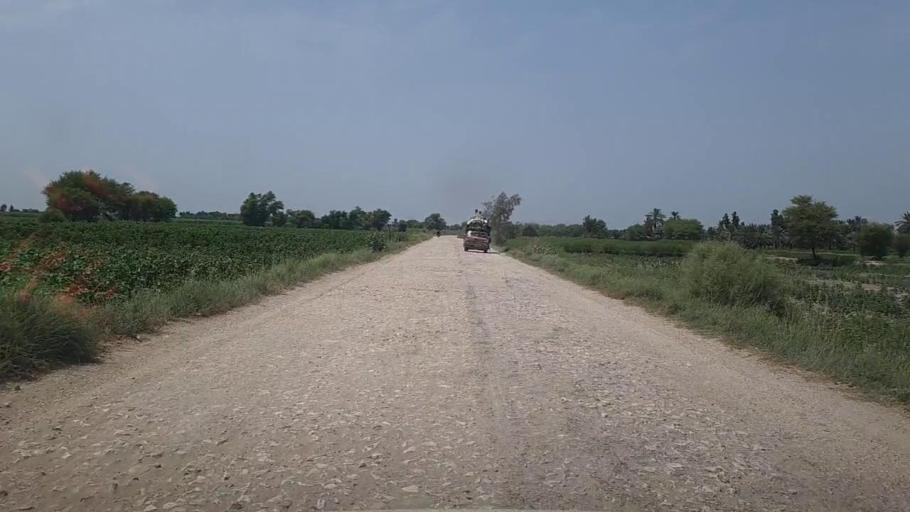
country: PK
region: Sindh
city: Pano Aqil
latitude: 27.8463
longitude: 69.1476
